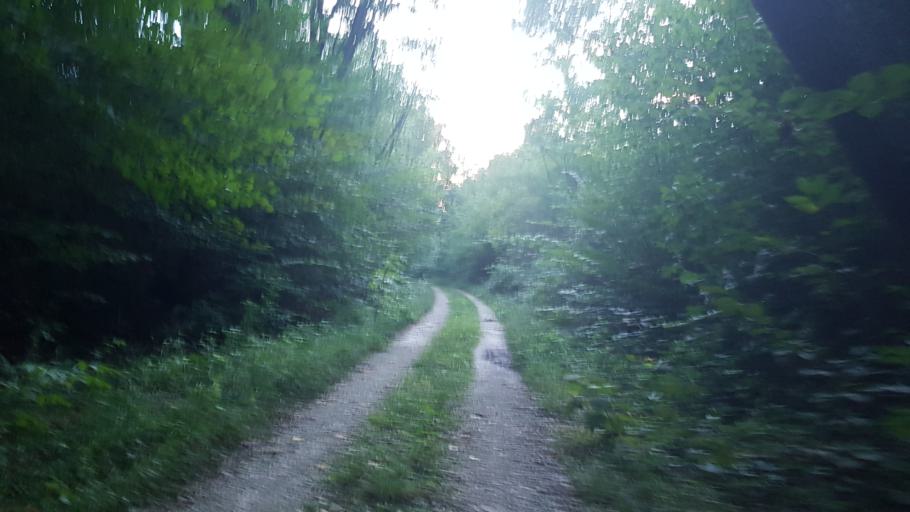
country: IT
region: Friuli Venezia Giulia
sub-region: Provincia di Gorizia
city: Mossa
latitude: 45.9460
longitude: 13.5346
